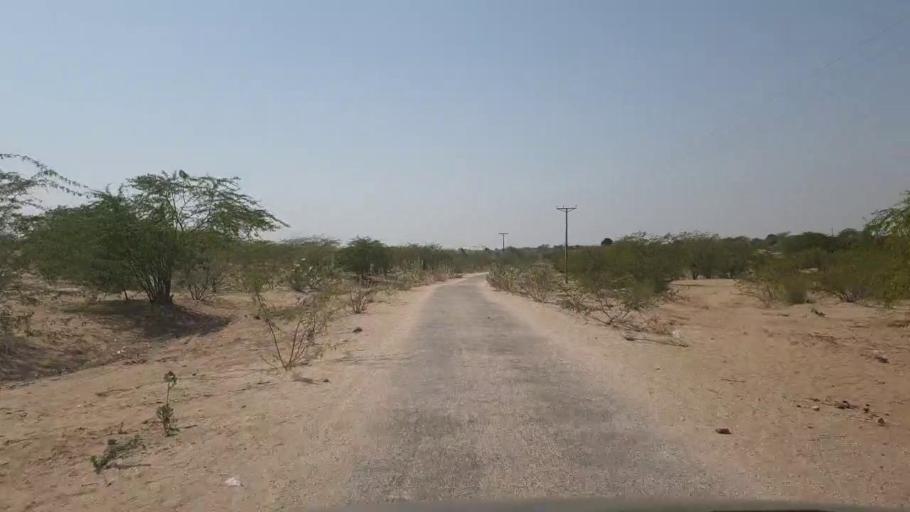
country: PK
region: Sindh
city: Chor
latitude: 25.5678
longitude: 70.1839
